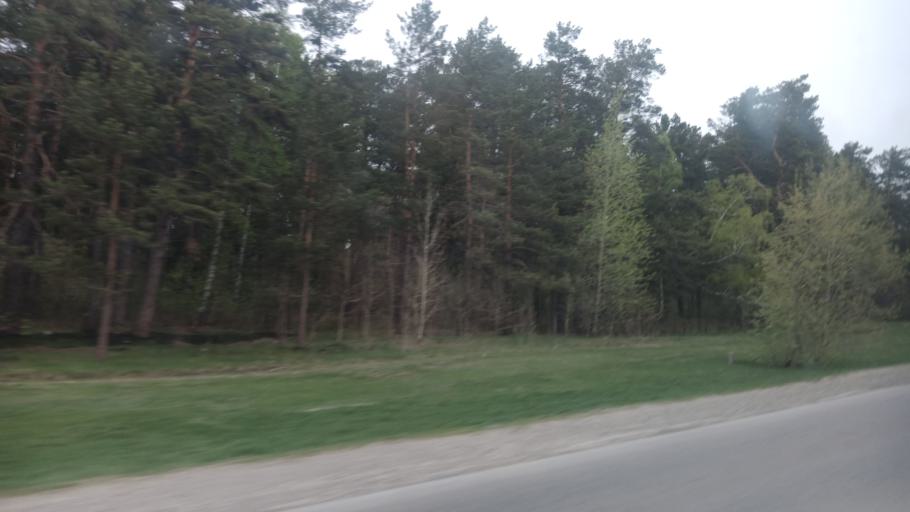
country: RU
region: Altai Krai
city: Yuzhnyy
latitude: 53.2638
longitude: 83.7074
